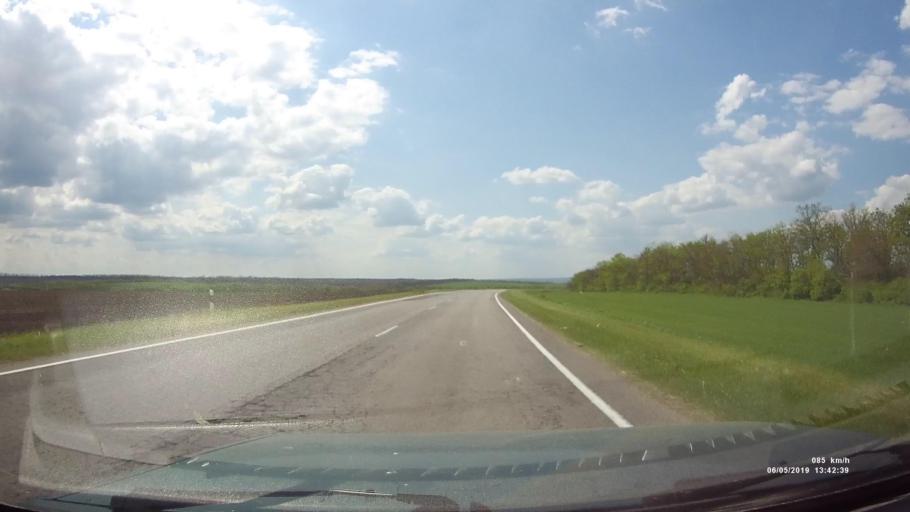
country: RU
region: Rostov
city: Semikarakorsk
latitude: 47.6594
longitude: 40.6535
